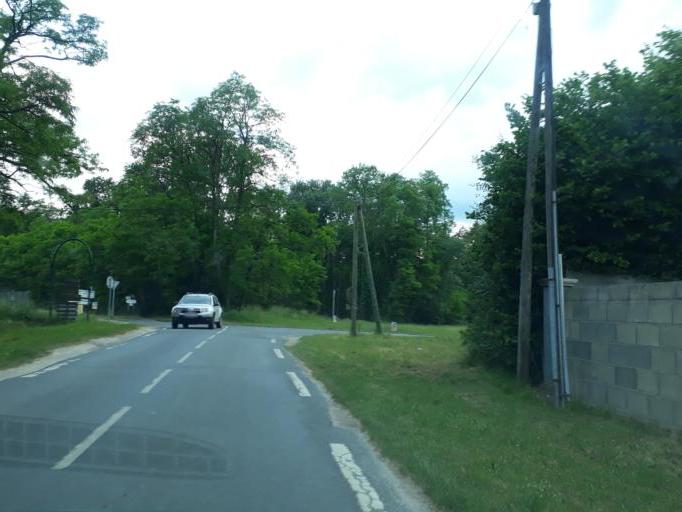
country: FR
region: Centre
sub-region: Departement du Loiret
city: Chaingy
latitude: 47.9159
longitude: 1.7879
